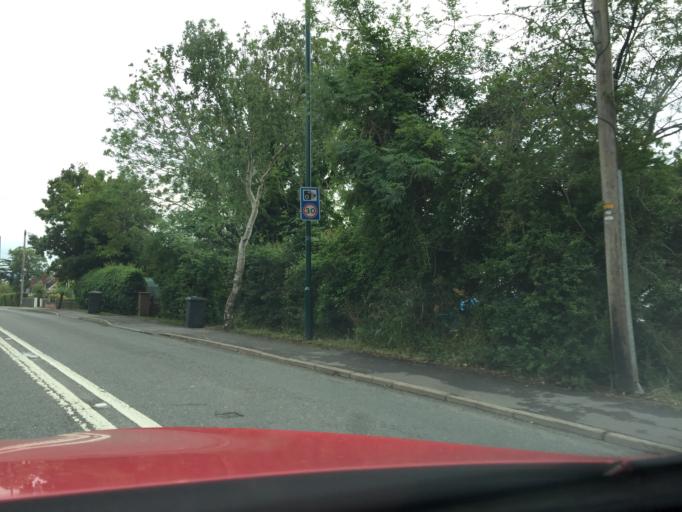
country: GB
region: England
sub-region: Warwickshire
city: Southam
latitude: 52.2592
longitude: -1.3890
